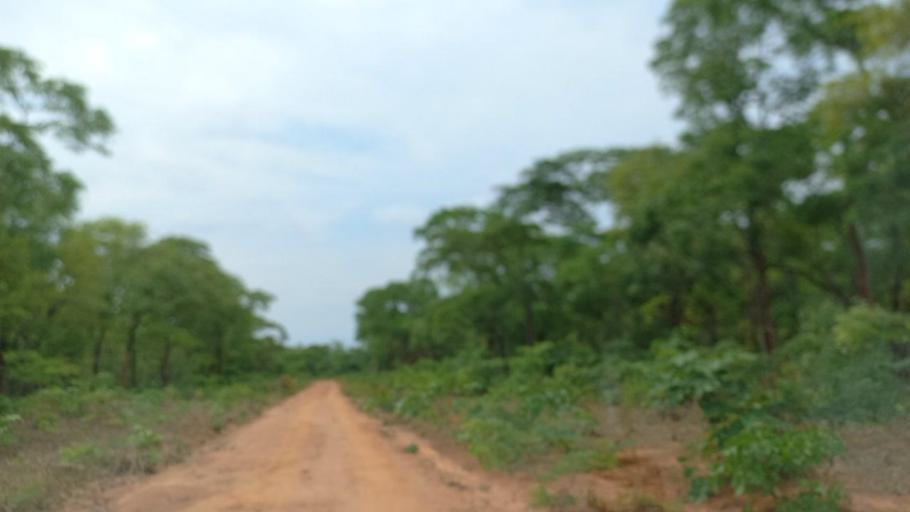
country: ZM
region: North-Western
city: Kalengwa
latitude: -13.6291
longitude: 24.9784
